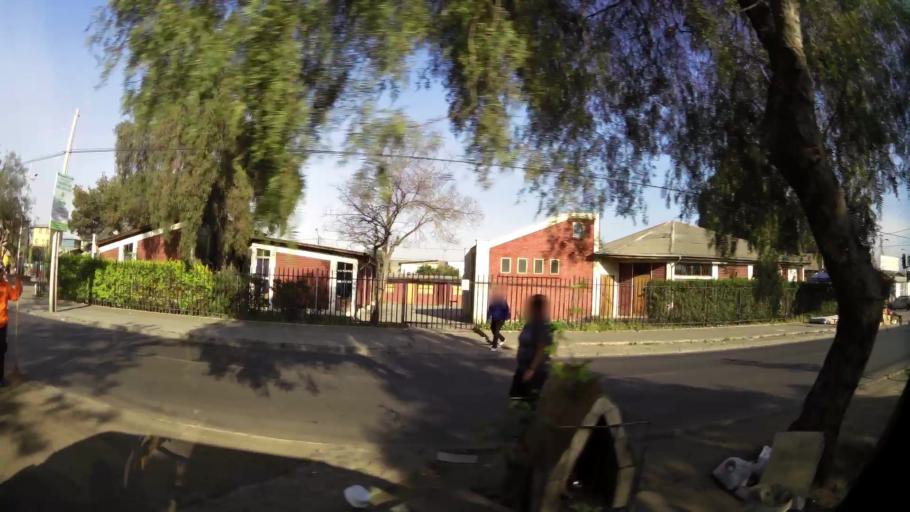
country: CL
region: Santiago Metropolitan
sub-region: Provincia de Santiago
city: Lo Prado
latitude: -33.4421
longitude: -70.7405
